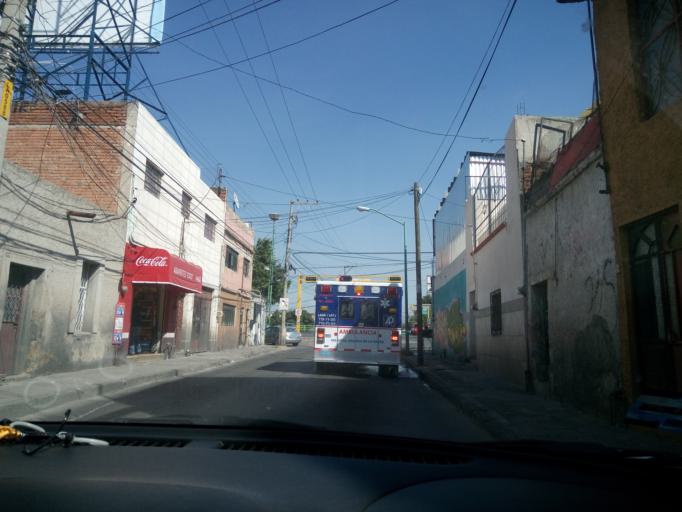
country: MX
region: Guanajuato
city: Leon
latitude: 21.1320
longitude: -101.6787
